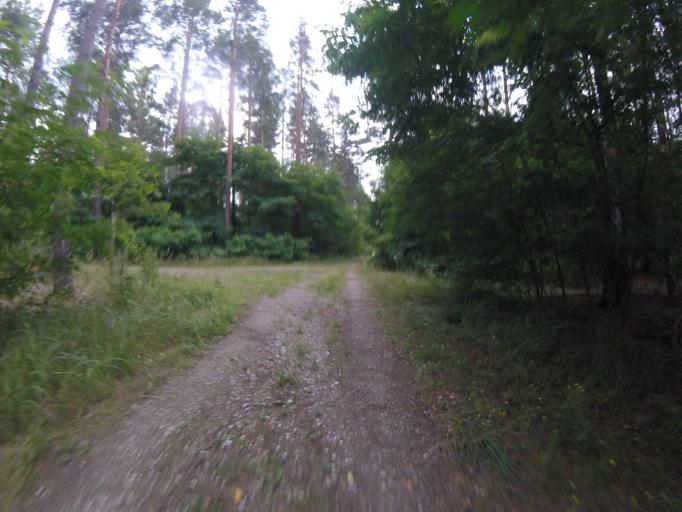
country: DE
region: Brandenburg
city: Schwerin
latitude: 52.1846
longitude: 13.6083
